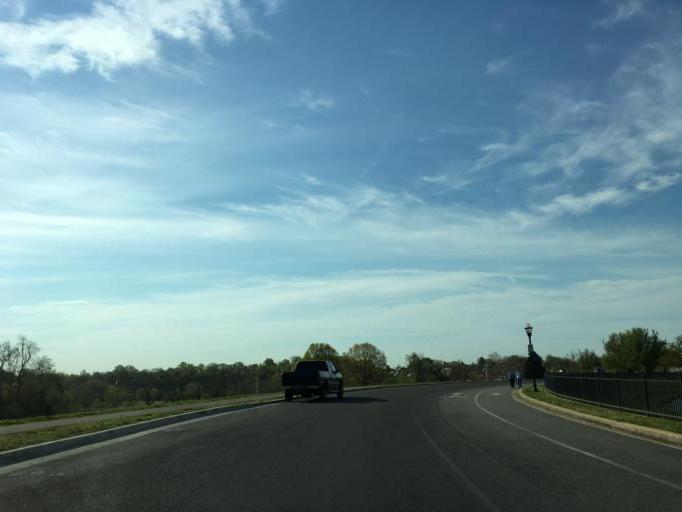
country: US
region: Maryland
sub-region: City of Baltimore
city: Baltimore
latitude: 39.3339
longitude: -76.5797
